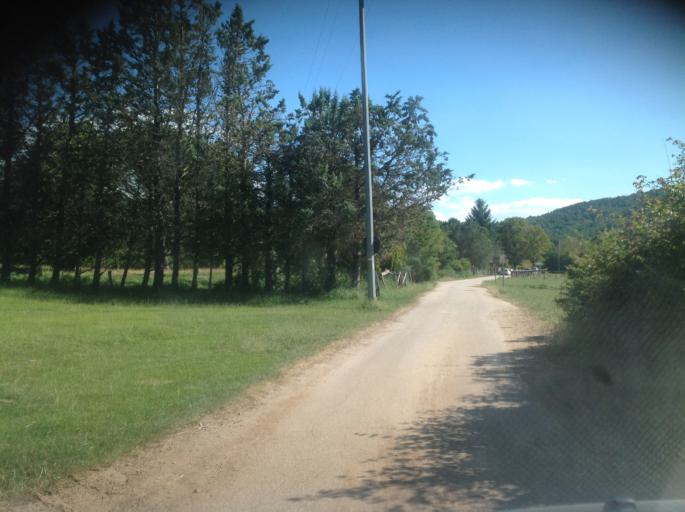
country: IT
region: Latium
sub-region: Provincia di Rieti
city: Limiti di Greccio
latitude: 42.4794
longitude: 12.7124
